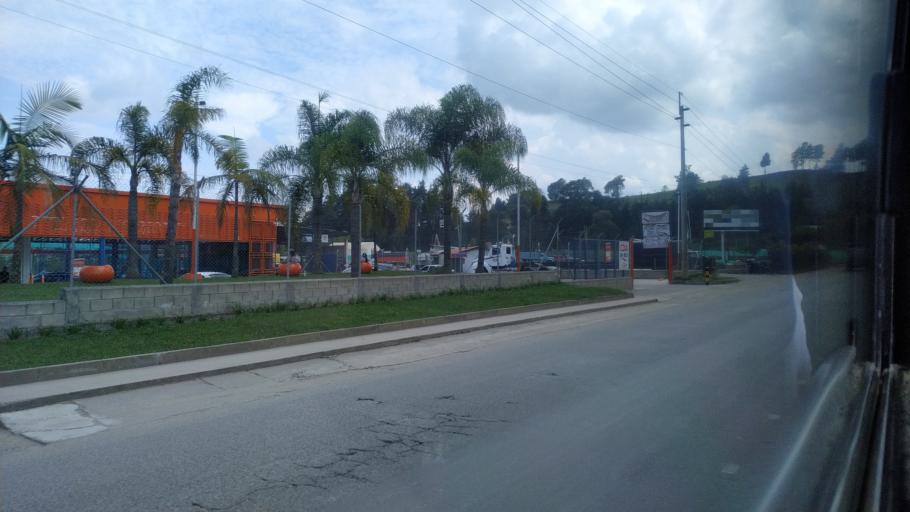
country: CO
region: Antioquia
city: Rionegro
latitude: 6.1732
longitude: -75.3700
